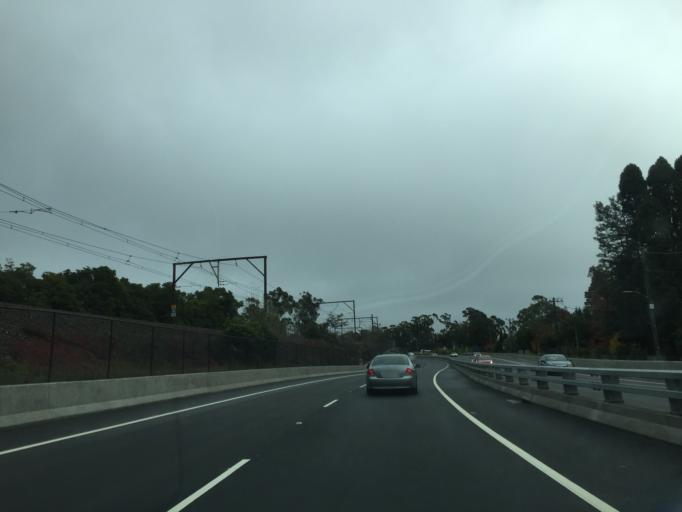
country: AU
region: New South Wales
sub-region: Blue Mountains Municipality
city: Hazelbrook
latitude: -33.7325
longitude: 150.4653
